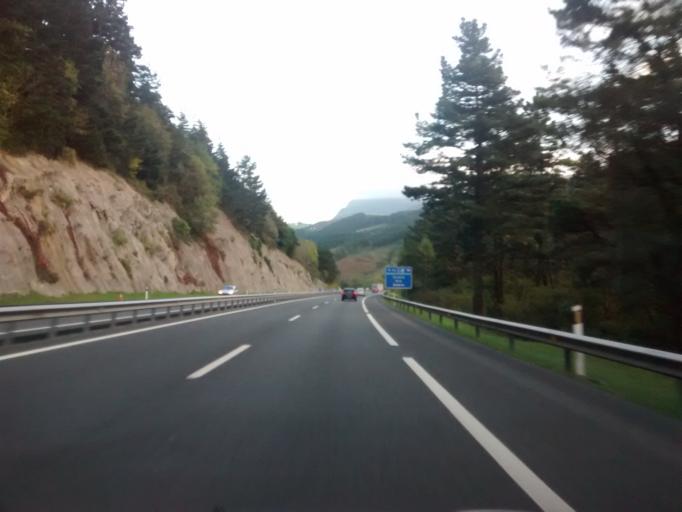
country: ES
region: Basque Country
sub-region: Provincia de Guipuzcoa
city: Deba
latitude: 43.2767
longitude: -2.3107
